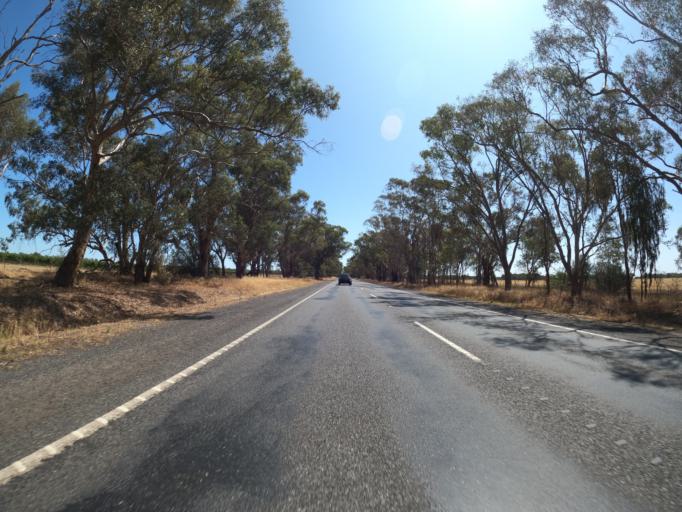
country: AU
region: New South Wales
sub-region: Corowa Shire
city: Corowa
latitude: -36.0595
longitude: 146.4217
